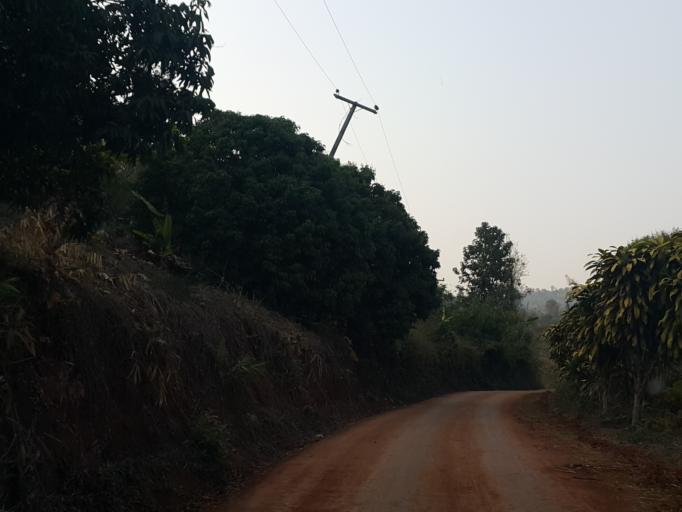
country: TH
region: Chiang Mai
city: Mae Taeng
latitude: 19.0729
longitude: 98.7715
